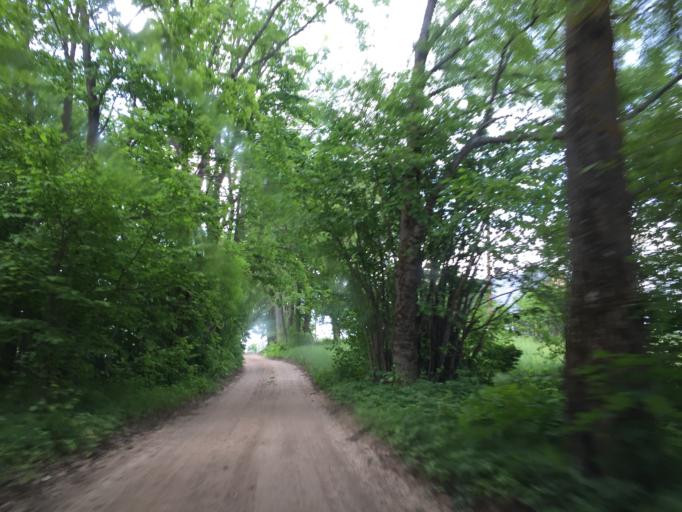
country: LV
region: Dagda
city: Dagda
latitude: 56.2797
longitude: 27.4702
